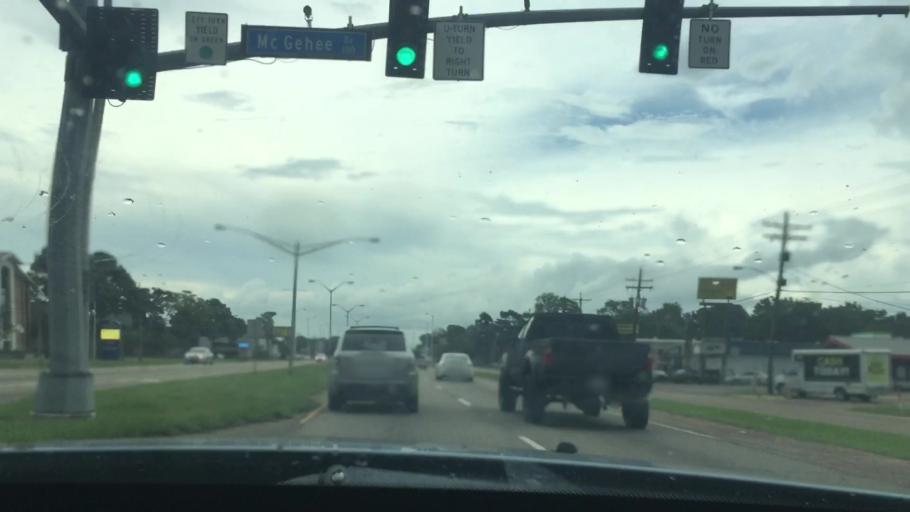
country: US
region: Louisiana
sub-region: East Baton Rouge Parish
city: Monticello
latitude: 30.4573
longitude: -91.0675
